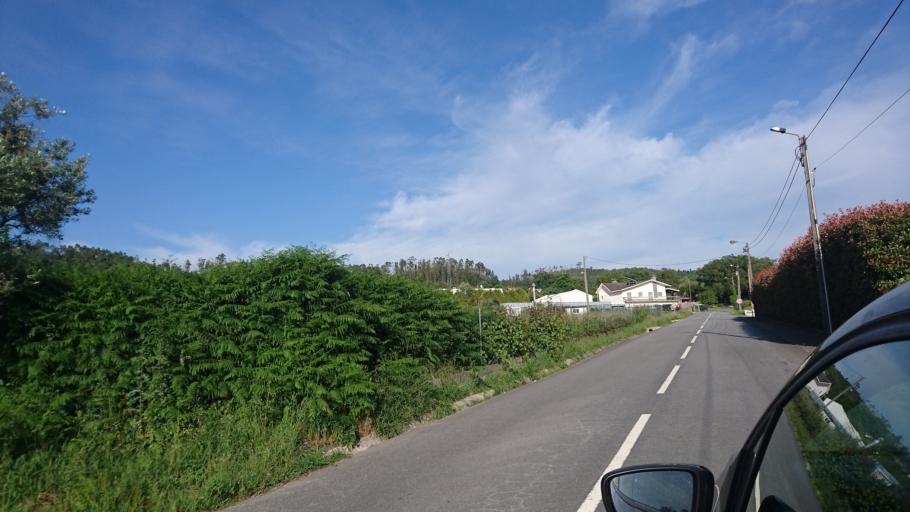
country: PT
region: Porto
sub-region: Paredes
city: Recarei
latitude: 41.1360
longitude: -8.3786
